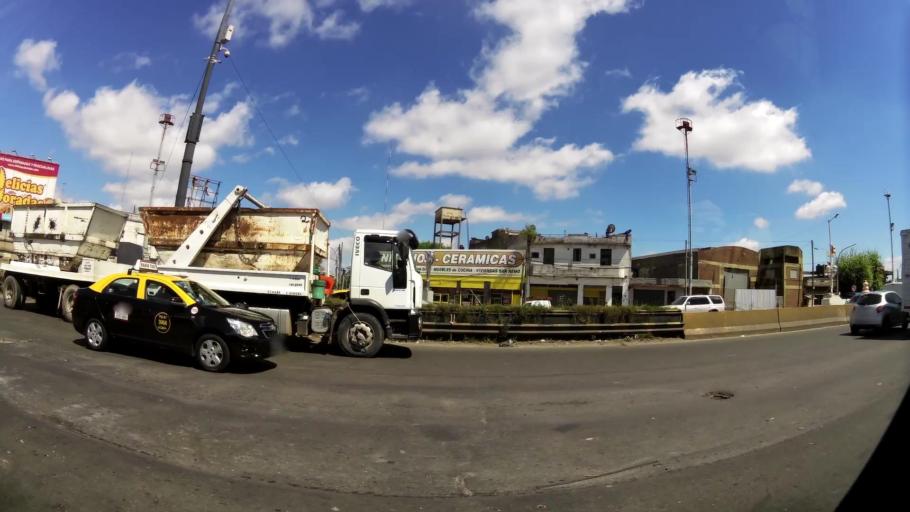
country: AR
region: Buenos Aires
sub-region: Partido de Lanus
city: Lanus
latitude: -34.6629
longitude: -58.4170
